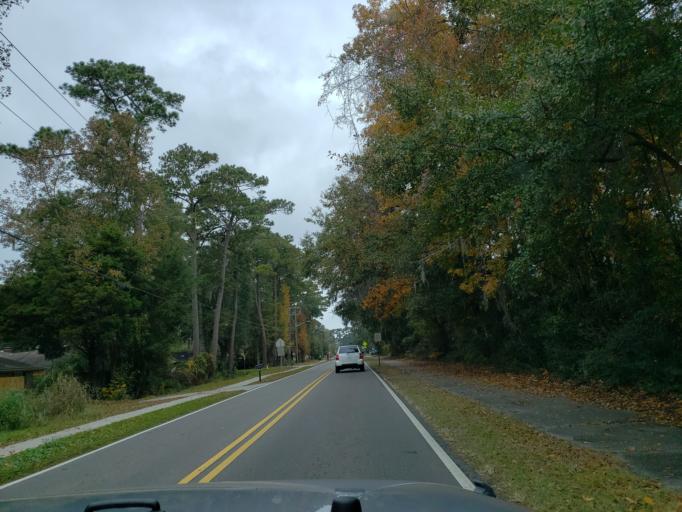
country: US
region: Georgia
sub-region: Chatham County
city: Wilmington Island
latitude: 32.0138
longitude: -80.9749
